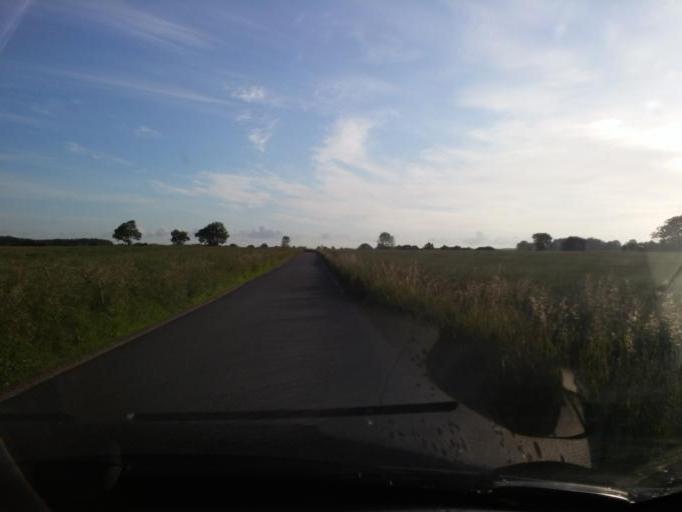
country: DK
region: South Denmark
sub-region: Kerteminde Kommune
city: Munkebo
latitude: 55.4076
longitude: 10.5624
